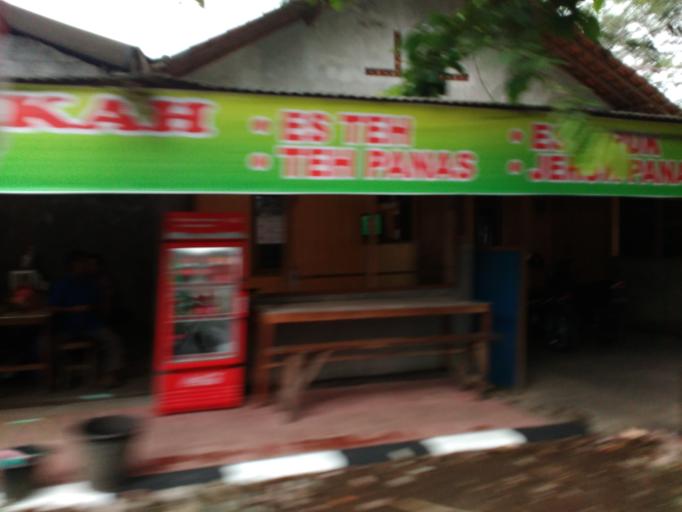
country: ID
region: Central Java
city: Boyolali
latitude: -7.5151
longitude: 110.5953
